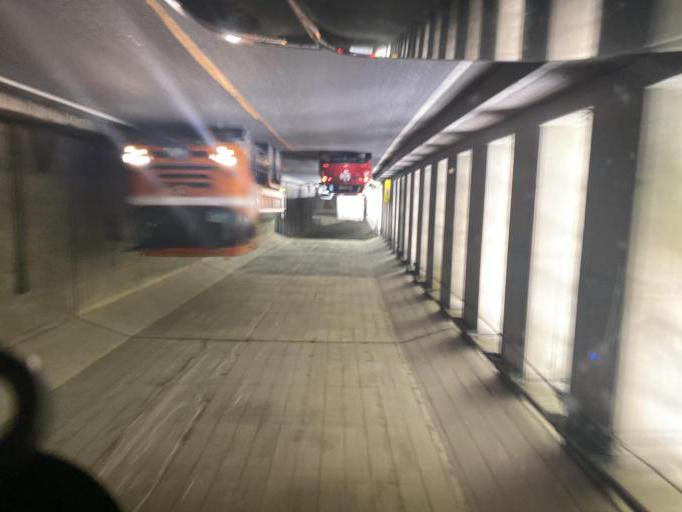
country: JP
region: Niigata
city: Itoigawa
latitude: 36.9451
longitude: 137.8582
